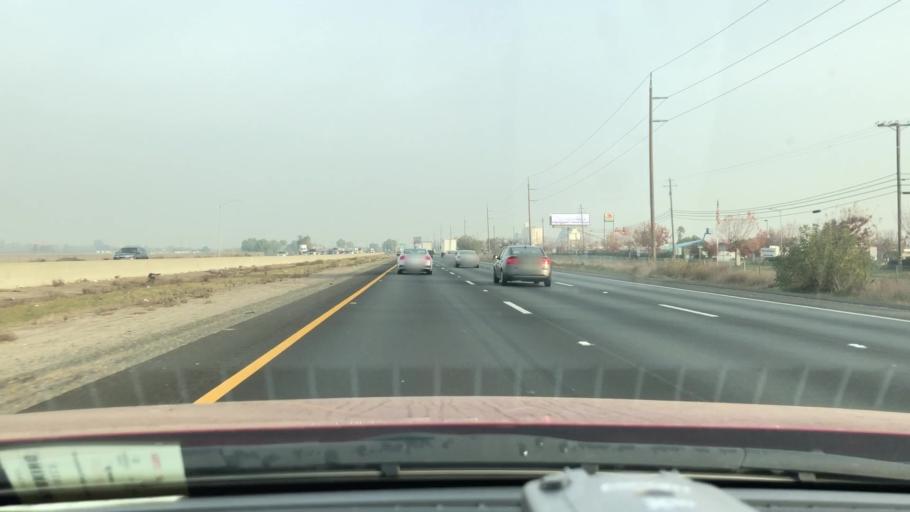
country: US
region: California
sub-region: San Joaquin County
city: French Camp
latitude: 37.8659
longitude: -121.2792
